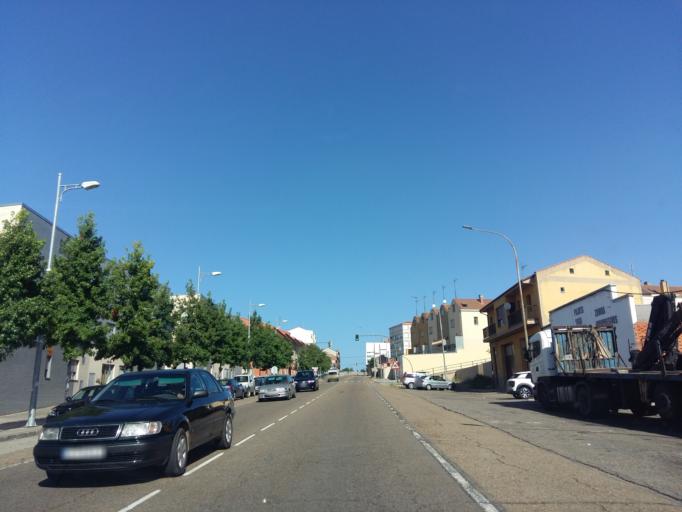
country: ES
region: Castille and Leon
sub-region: Provincia de Leon
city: Astorga
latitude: 42.4538
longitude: -6.0577
